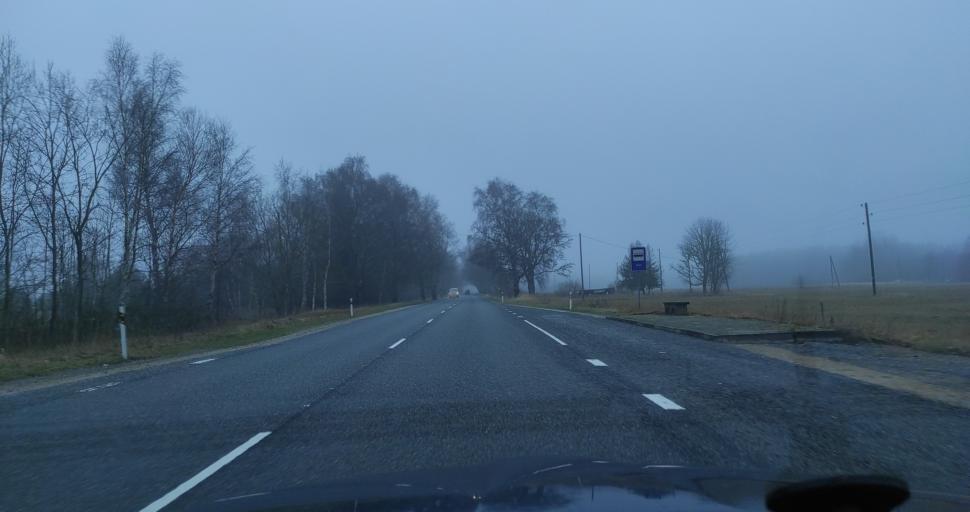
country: LV
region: Alsunga
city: Alsunga
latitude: 56.9983
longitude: 21.3796
